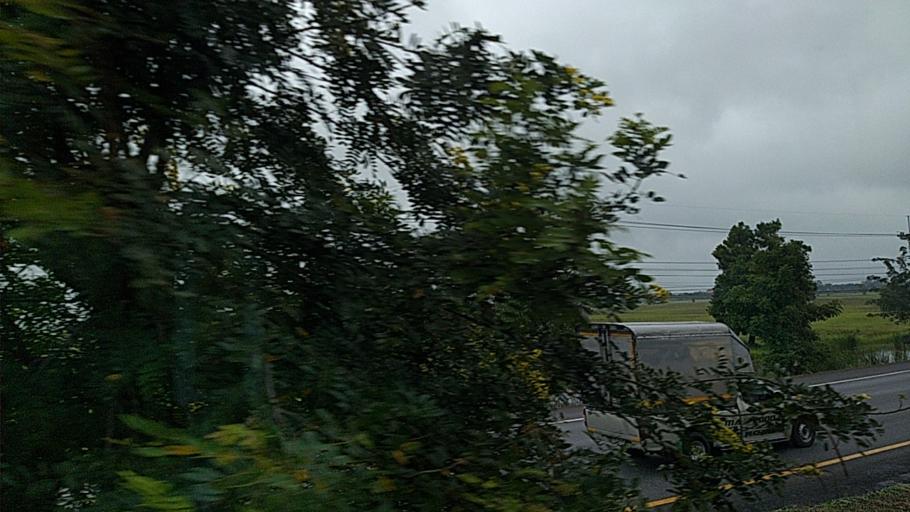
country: TH
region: Nakhon Ratchasima
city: Phimai
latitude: 15.3314
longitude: 102.4389
